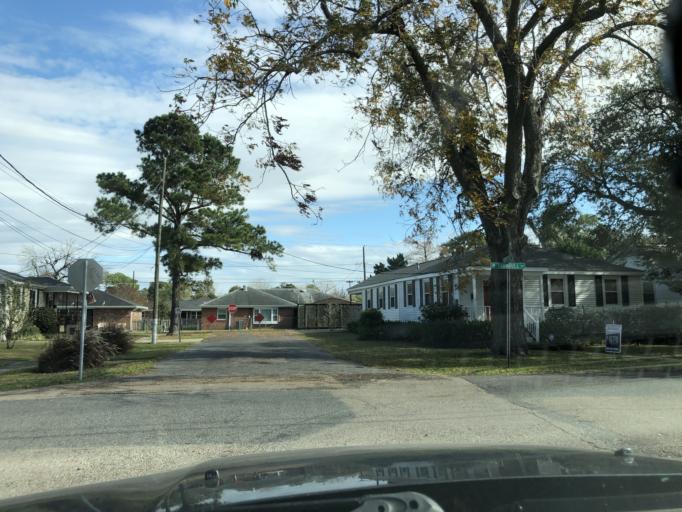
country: US
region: Louisiana
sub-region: Jefferson Parish
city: Metairie Terrace
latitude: 29.9831
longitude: -90.1681
